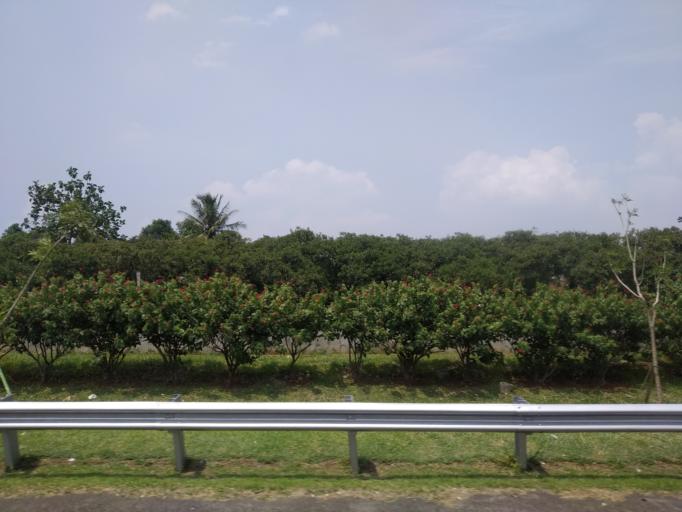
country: ID
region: West Java
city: Citeureup
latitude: -6.4818
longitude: 106.8745
